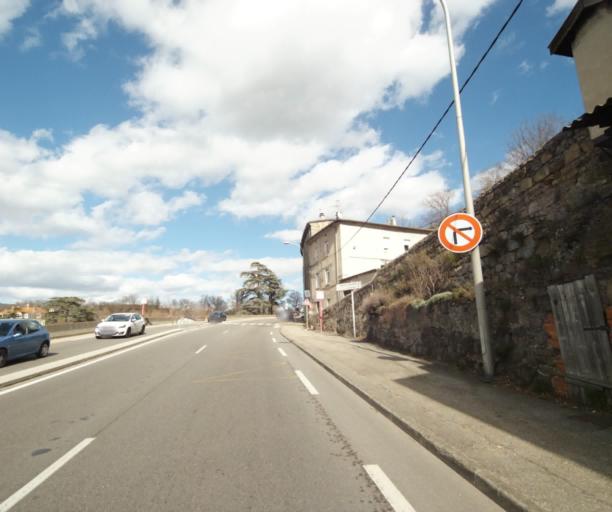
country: FR
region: Rhone-Alpes
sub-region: Departement de l'Ardeche
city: Annonay
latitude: 45.2518
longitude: 4.6819
